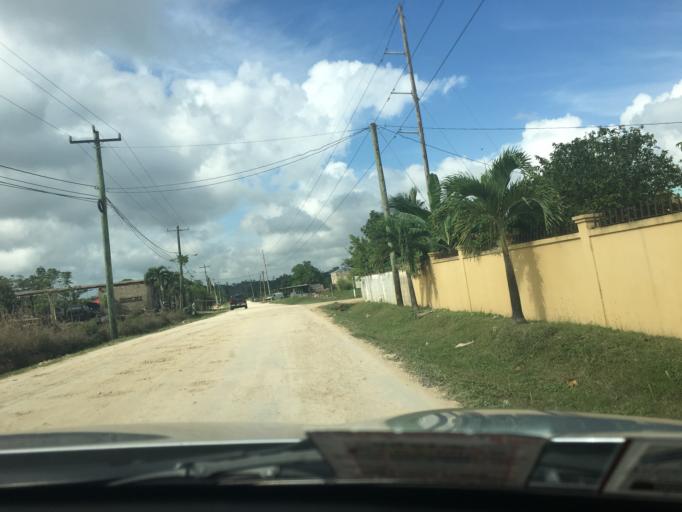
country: BZ
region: Cayo
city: Belmopan
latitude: 17.2507
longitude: -88.7873
